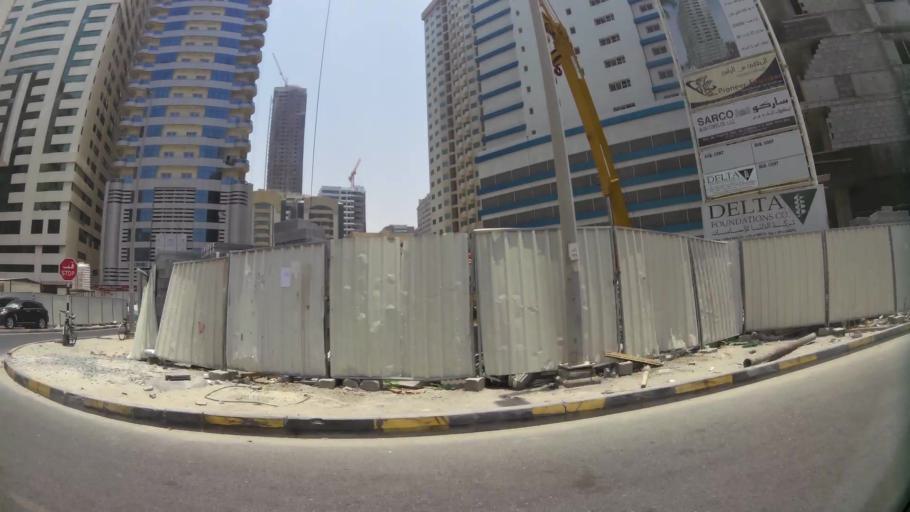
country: AE
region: Ash Shariqah
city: Sharjah
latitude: 25.3300
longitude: 55.3748
